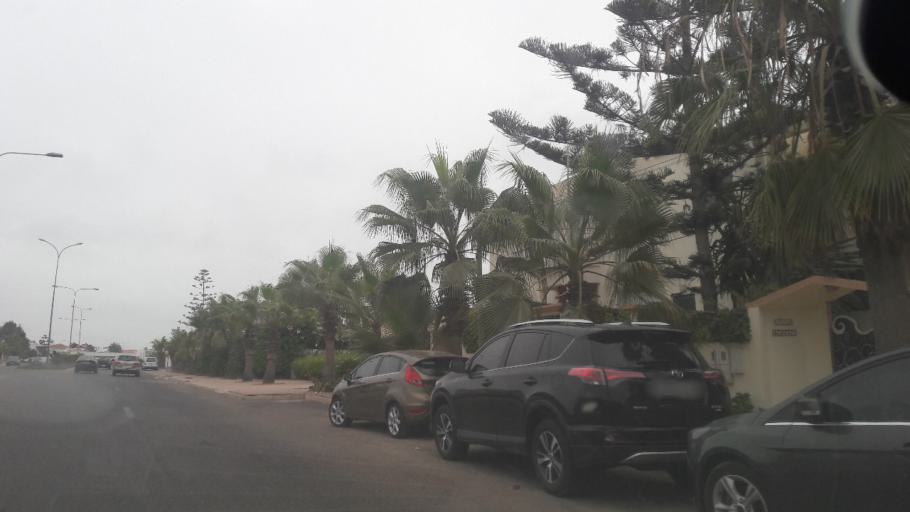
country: MA
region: Souss-Massa-Draa
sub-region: Agadir-Ida-ou-Tnan
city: Agadir
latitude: 30.3913
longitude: -9.5943
